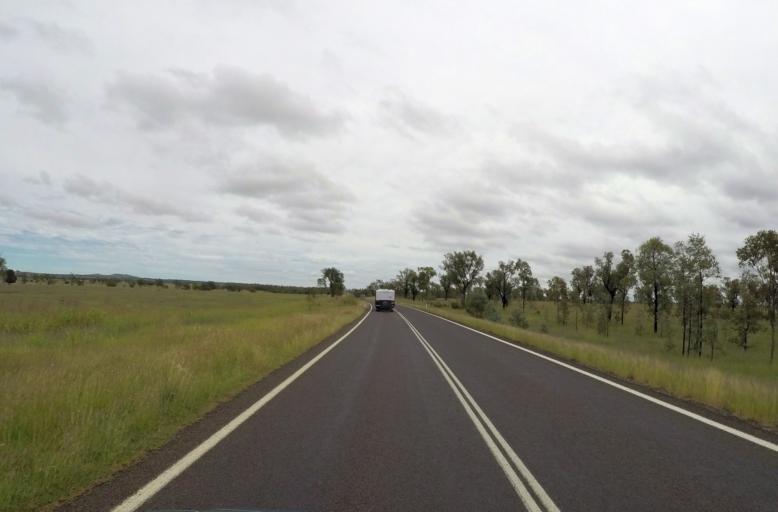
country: AU
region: Queensland
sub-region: Maranoa
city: Roma
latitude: -26.3916
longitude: 148.7846
